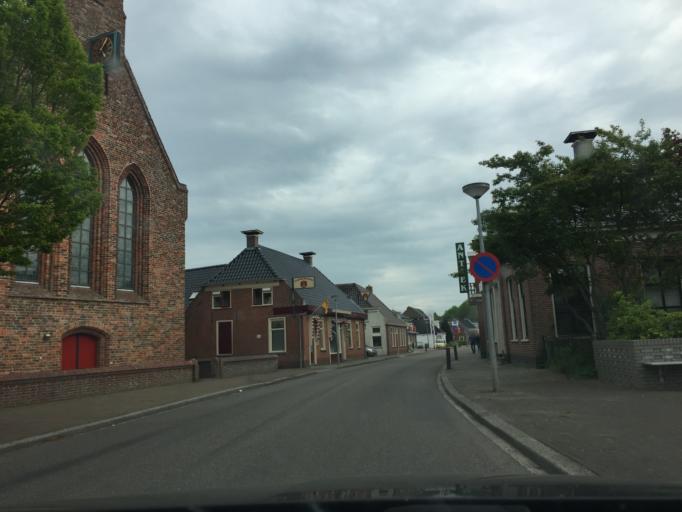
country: NL
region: Groningen
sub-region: Gemeente Zuidhorn
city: Aduard
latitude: 53.2566
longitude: 6.4596
